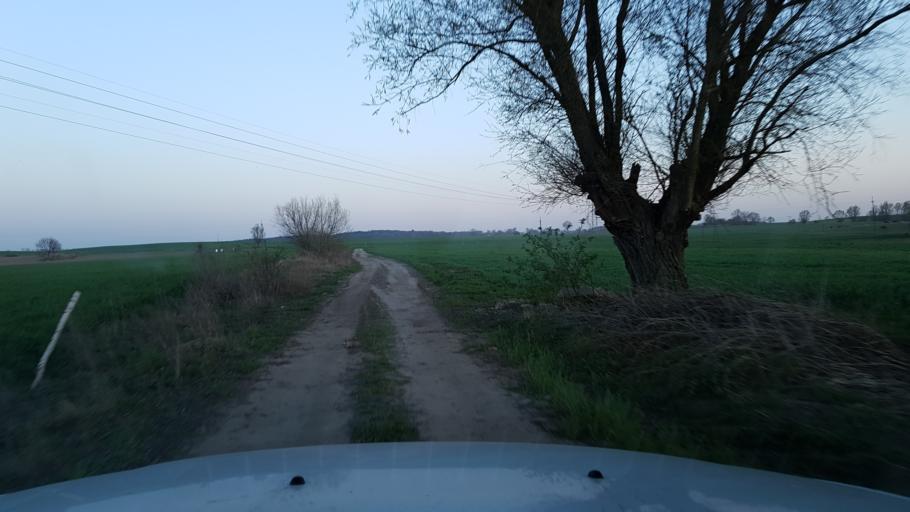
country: PL
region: West Pomeranian Voivodeship
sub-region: Powiat bialogardzki
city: Bialogard
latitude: 53.9649
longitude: 15.9559
